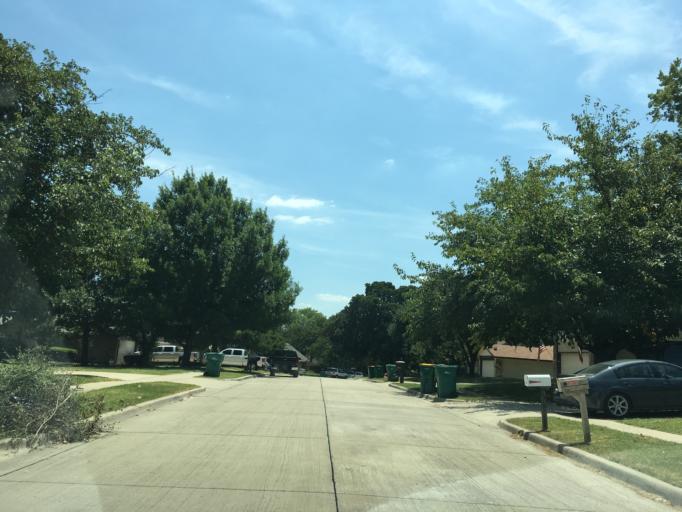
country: US
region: Texas
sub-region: Denton County
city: Lewisville
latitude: 33.0296
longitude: -97.0030
